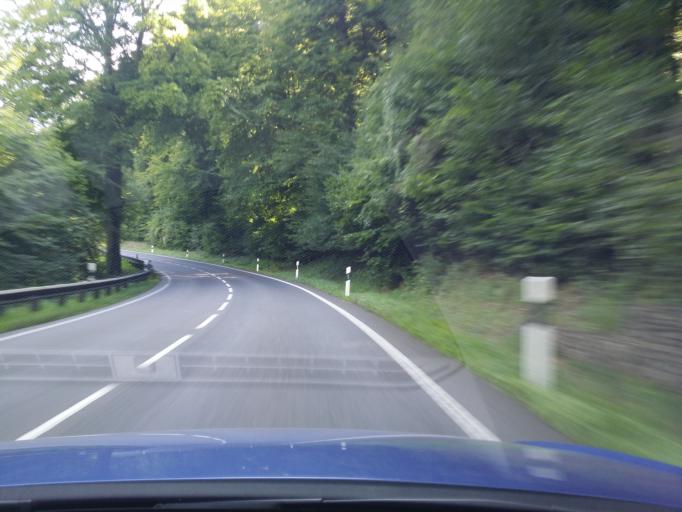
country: LU
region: Luxembourg
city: Rollingen
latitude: 49.7261
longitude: 6.0987
